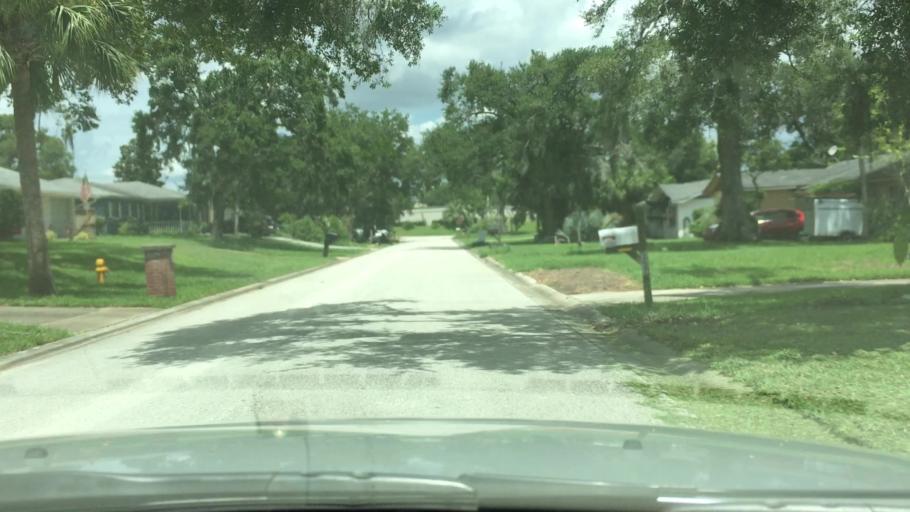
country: US
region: Florida
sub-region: Volusia County
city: Ormond Beach
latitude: 29.2659
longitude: -81.0767
